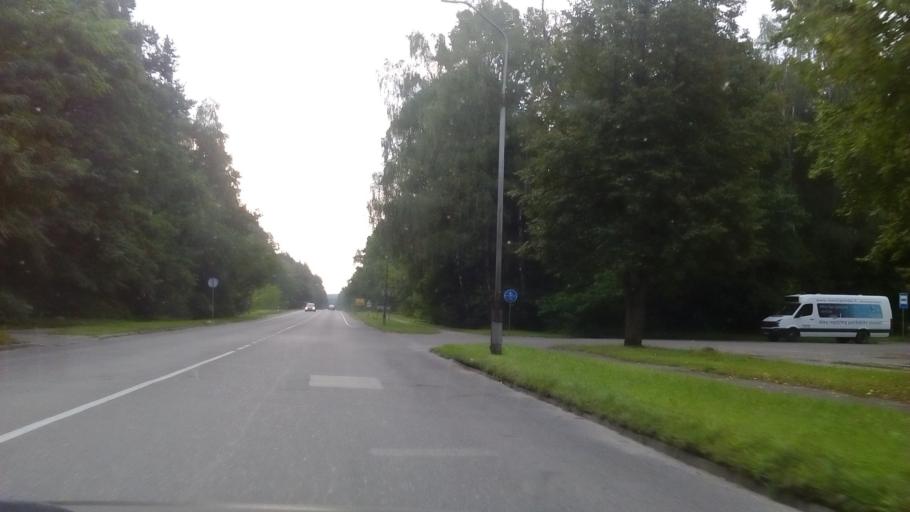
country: LT
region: Alytaus apskritis
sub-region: Alytus
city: Alytus
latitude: 54.3790
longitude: 24.0644
